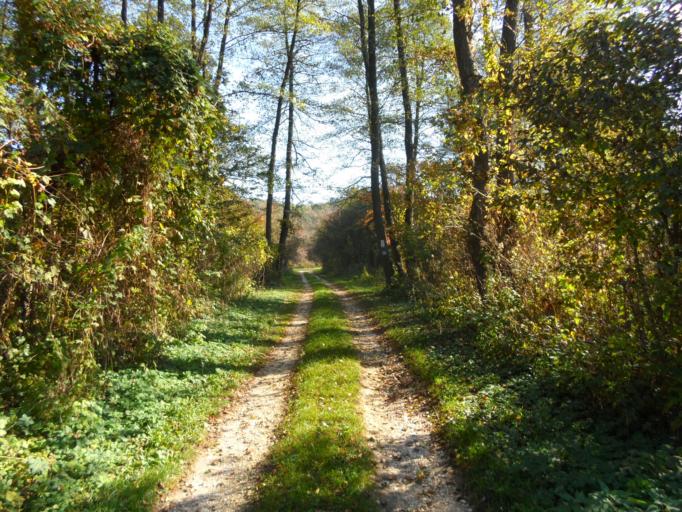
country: HU
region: Veszprem
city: Ajka
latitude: 47.2195
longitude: 17.5641
